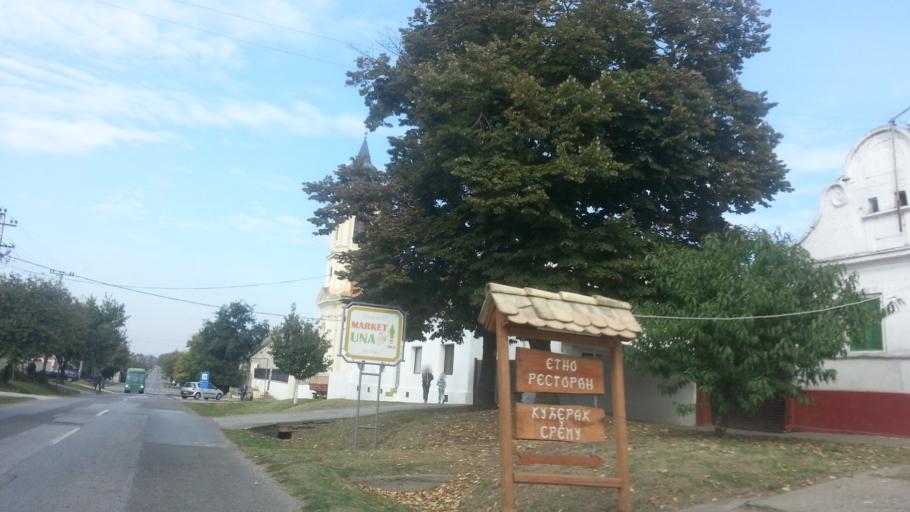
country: RS
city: Surduk
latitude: 45.0701
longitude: 20.3267
